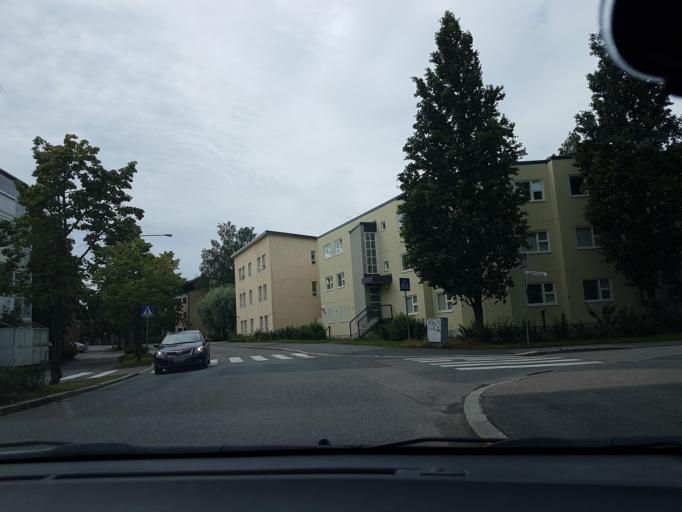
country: FI
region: Uusimaa
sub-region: Helsinki
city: Vantaa
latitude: 60.2566
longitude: 25.0114
